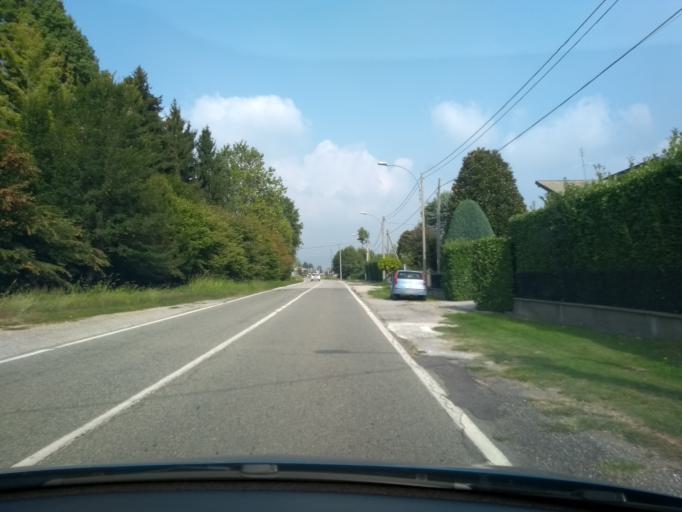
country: IT
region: Piedmont
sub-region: Provincia di Torino
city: Oglianico
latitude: 45.3491
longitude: 7.6923
